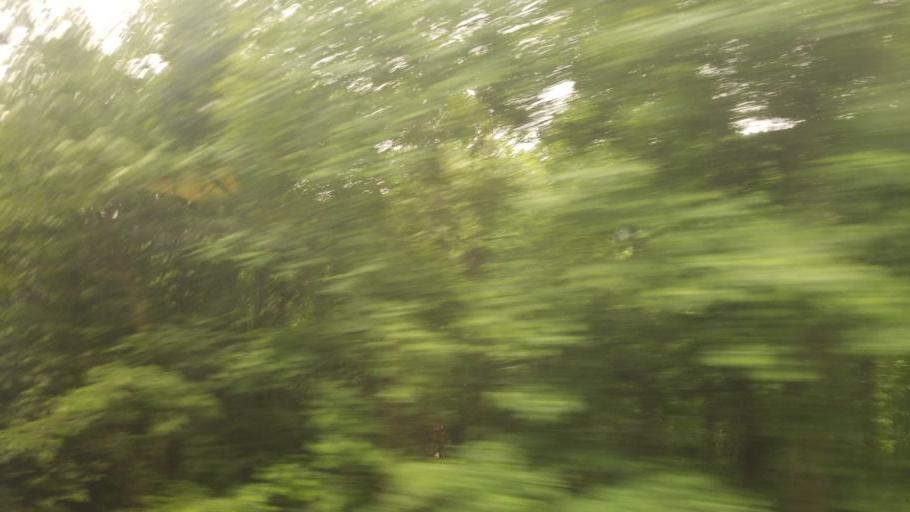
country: US
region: Pennsylvania
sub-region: Somerset County
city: Milford
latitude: 39.8292
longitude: -79.2753
